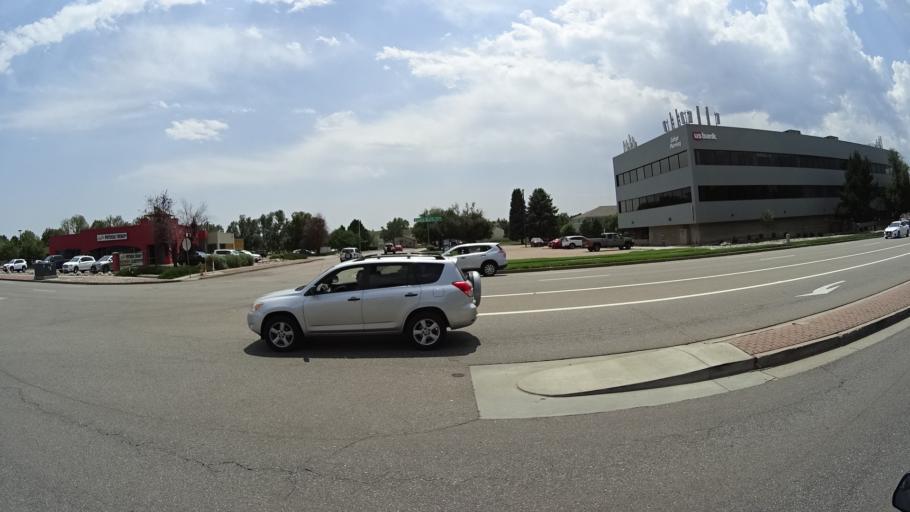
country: US
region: Colorado
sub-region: El Paso County
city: Cimarron Hills
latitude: 38.8909
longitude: -104.7622
